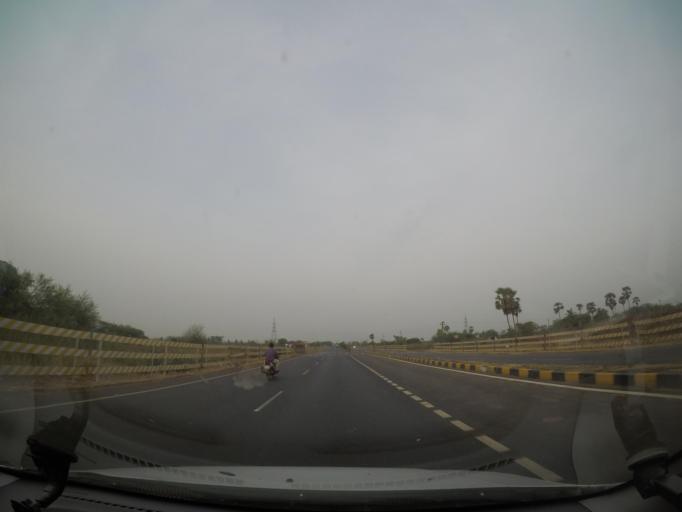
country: IN
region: Andhra Pradesh
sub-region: Krishna
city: Gannavaram
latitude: 16.6198
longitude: 80.9301
